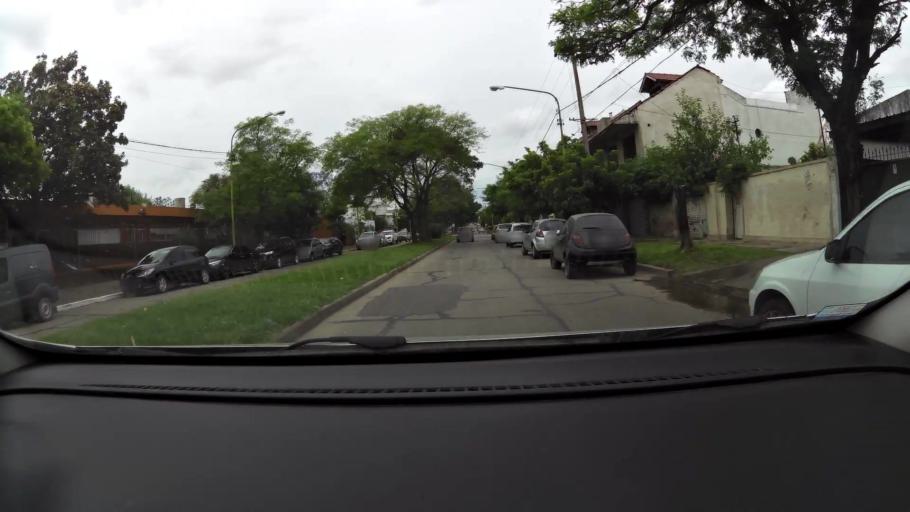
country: AR
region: Buenos Aires
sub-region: Partido de Campana
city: Campana
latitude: -34.1701
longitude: -58.9573
